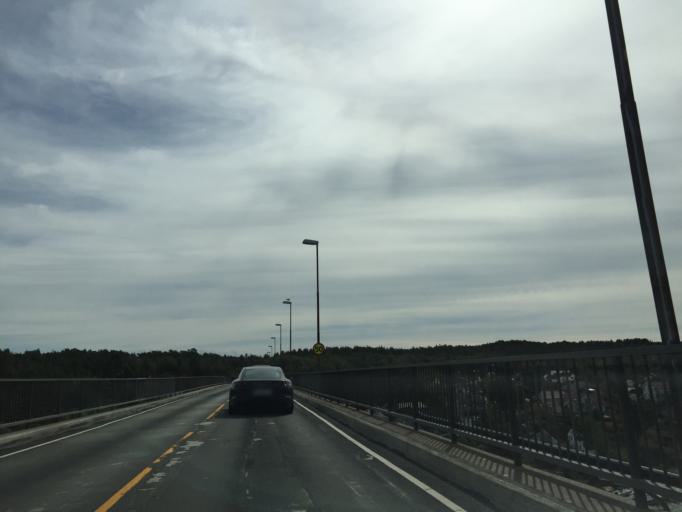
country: NO
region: Ostfold
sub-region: Fredrikstad
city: Fredrikstad
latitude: 59.1463
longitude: 10.9433
